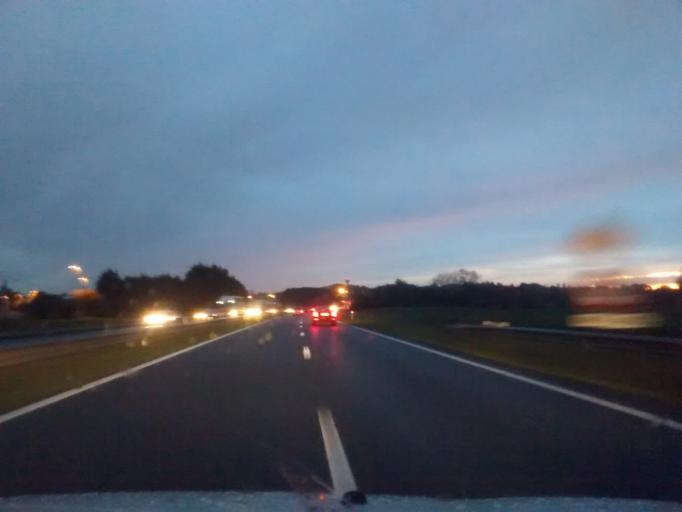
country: FR
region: Brittany
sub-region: Departement des Cotes-d'Armor
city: Tremuson
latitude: 48.5264
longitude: -2.8648
